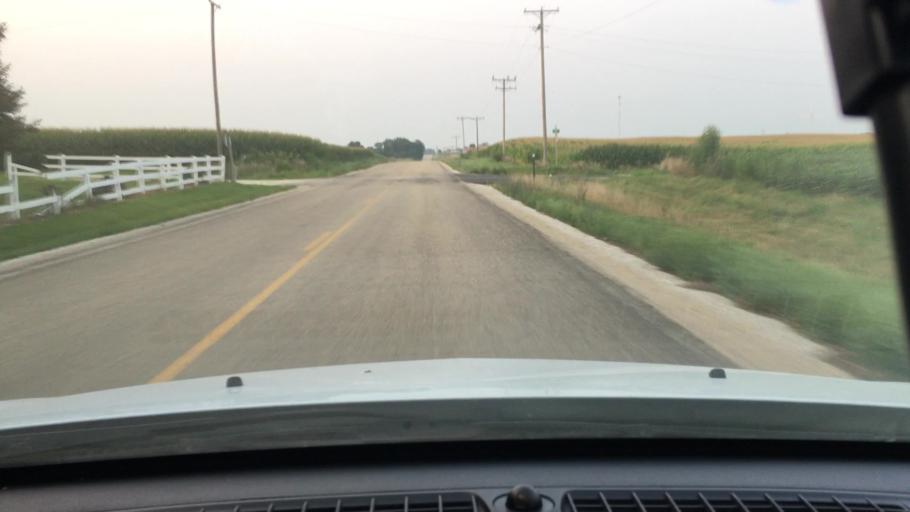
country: US
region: Illinois
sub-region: DeKalb County
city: Waterman
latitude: 41.8204
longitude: -88.7733
